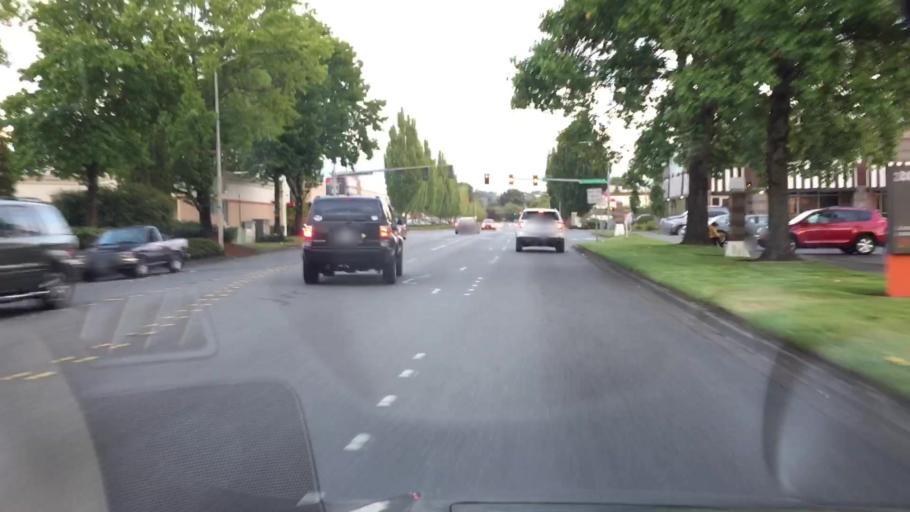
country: US
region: Washington
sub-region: King County
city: Tukwila
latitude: 47.4558
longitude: -122.2557
